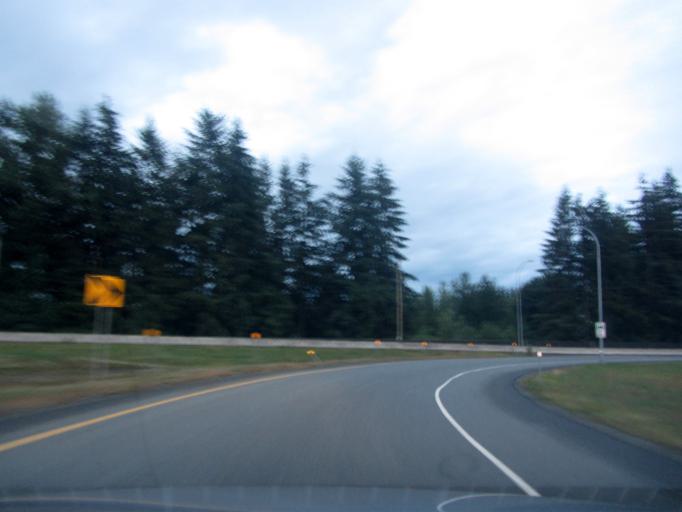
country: US
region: Washington
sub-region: Whatcom County
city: Sumas
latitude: 49.0362
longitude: -122.3355
